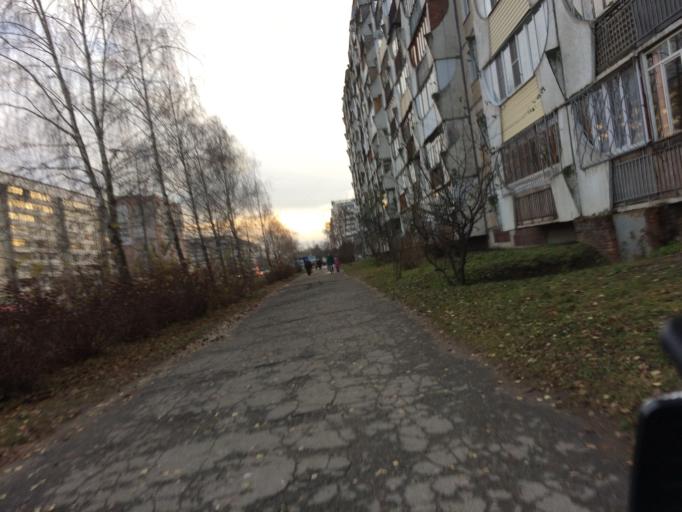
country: RU
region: Mariy-El
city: Yoshkar-Ola
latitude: 56.6327
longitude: 47.9189
